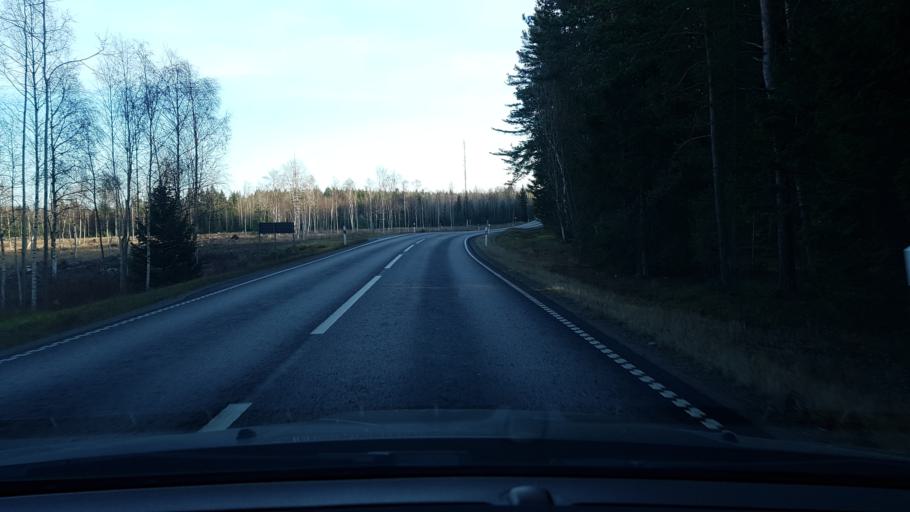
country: SE
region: Stockholm
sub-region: Norrtalje Kommun
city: Nykvarn
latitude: 59.7409
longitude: 18.2267
